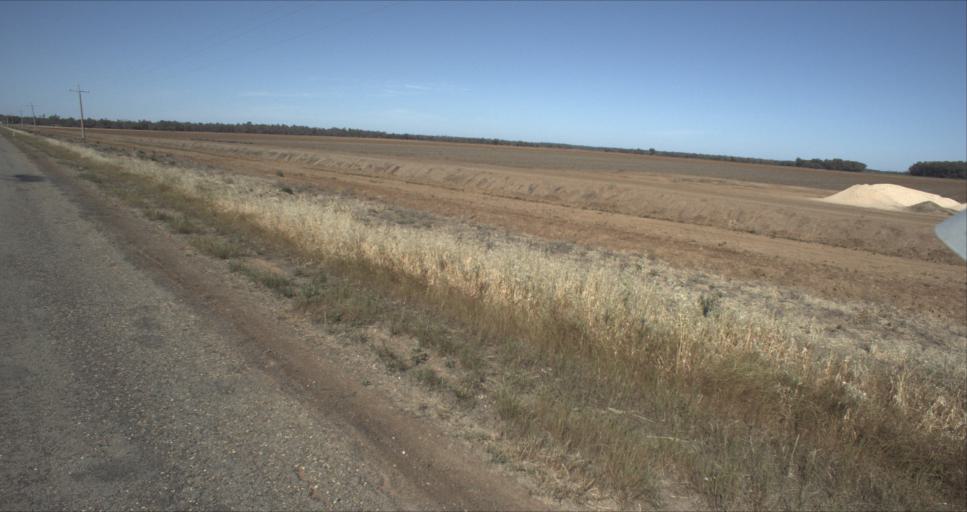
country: AU
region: New South Wales
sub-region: Leeton
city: Leeton
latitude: -34.5945
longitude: 146.2590
